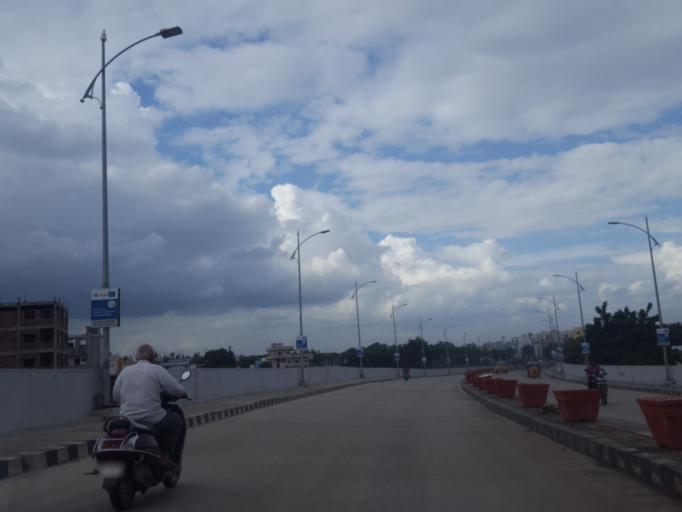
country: IN
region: Telangana
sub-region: Medak
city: Serilingampalle
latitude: 17.4823
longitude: 78.3111
